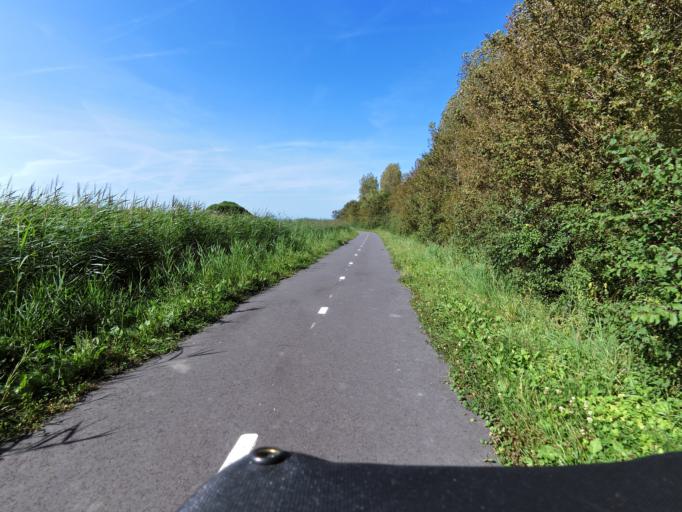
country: NL
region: South Holland
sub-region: Gemeente Goeree-Overflakkee
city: Dirksland
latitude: 51.7377
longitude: 4.0829
